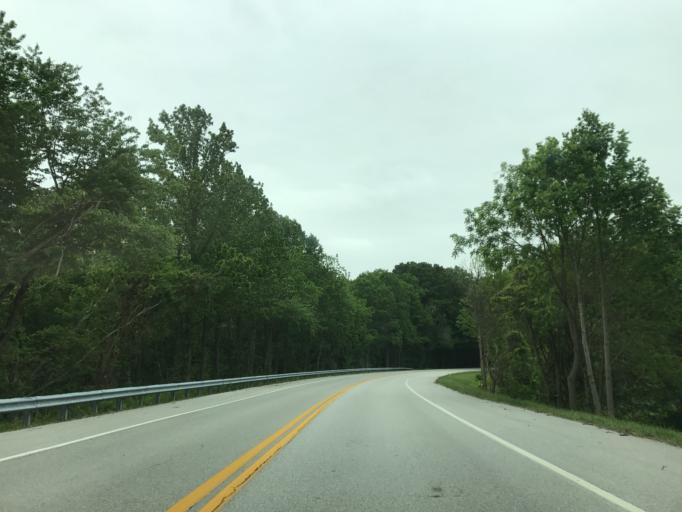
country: US
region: Pennsylvania
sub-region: York County
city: New Freedom
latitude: 39.7206
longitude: -76.6499
